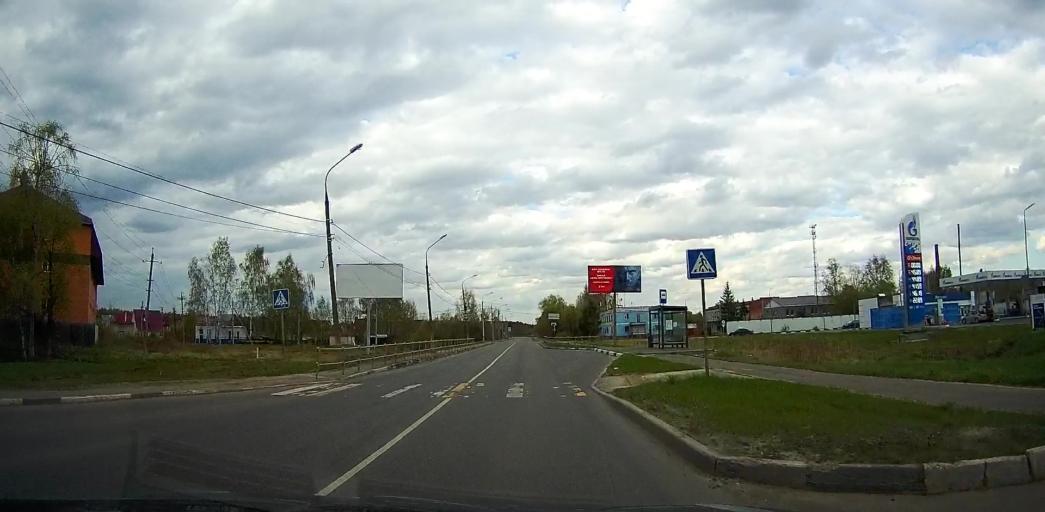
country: RU
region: Moskovskaya
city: Pavlovskiy Posad
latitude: 55.7926
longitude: 38.6497
